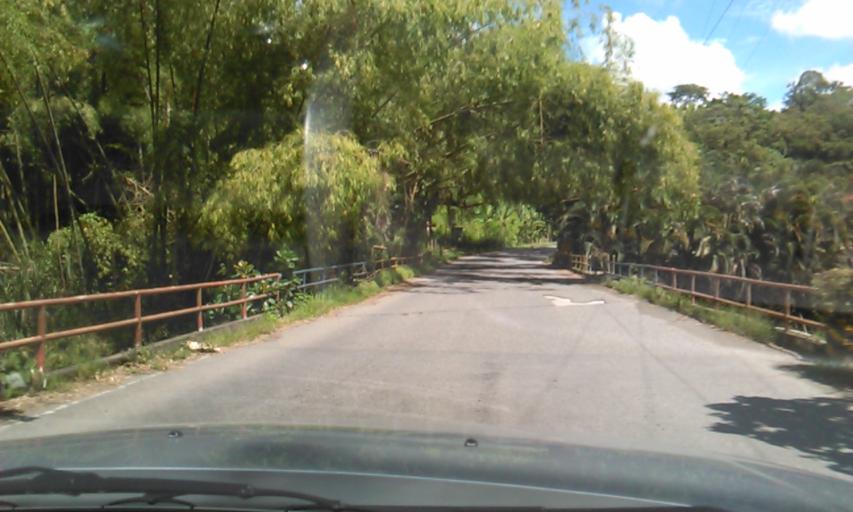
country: CO
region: Quindio
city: Cordoba
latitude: 4.4047
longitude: -75.7322
